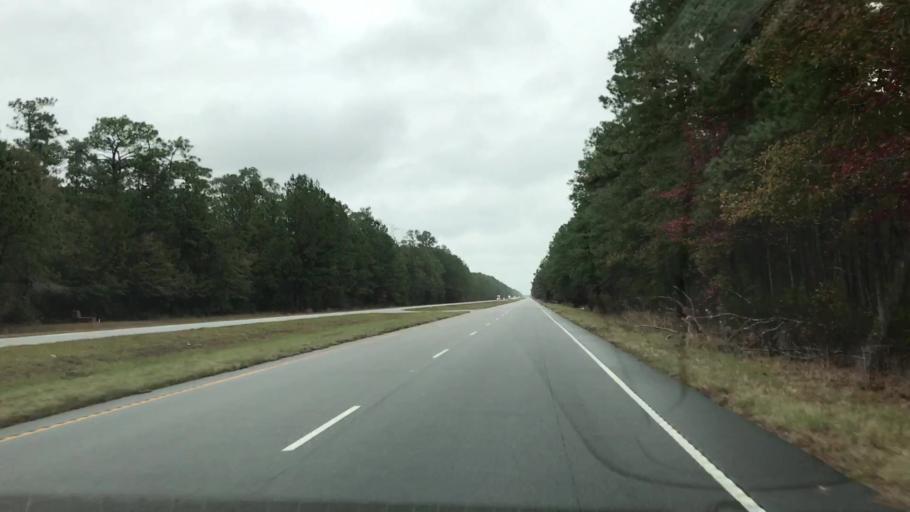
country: US
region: South Carolina
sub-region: Charleston County
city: Awendaw
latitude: 33.1399
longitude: -79.4401
